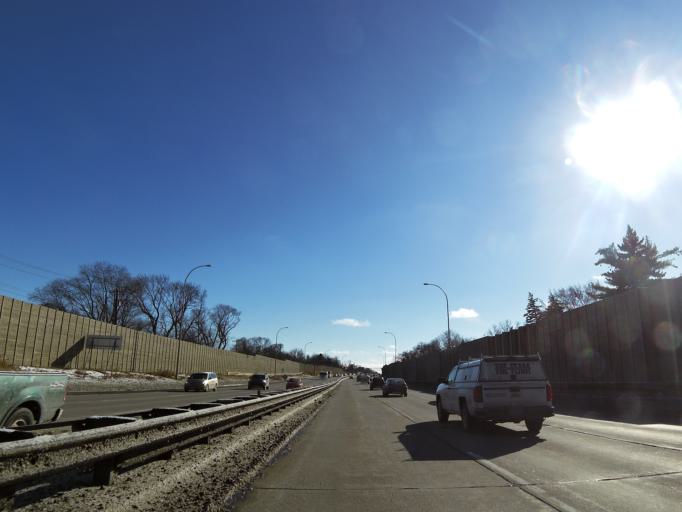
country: US
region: Minnesota
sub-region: Hennepin County
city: Saint Louis Park
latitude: 44.9235
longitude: -93.3494
